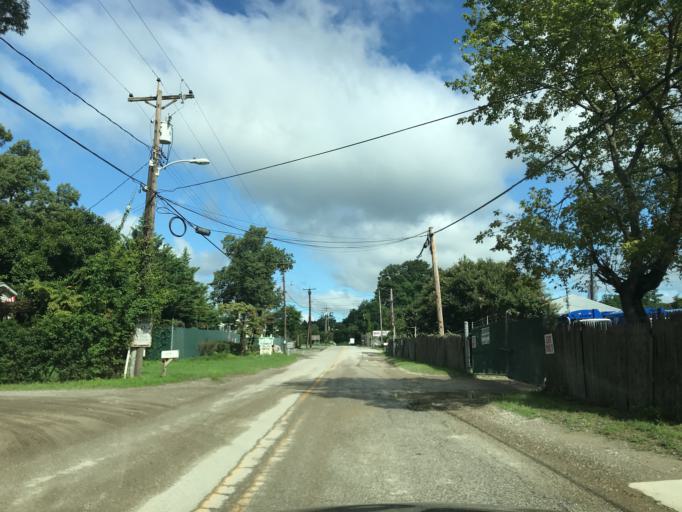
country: US
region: Maryland
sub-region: Anne Arundel County
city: Pasadena
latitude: 39.1186
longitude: -76.5647
